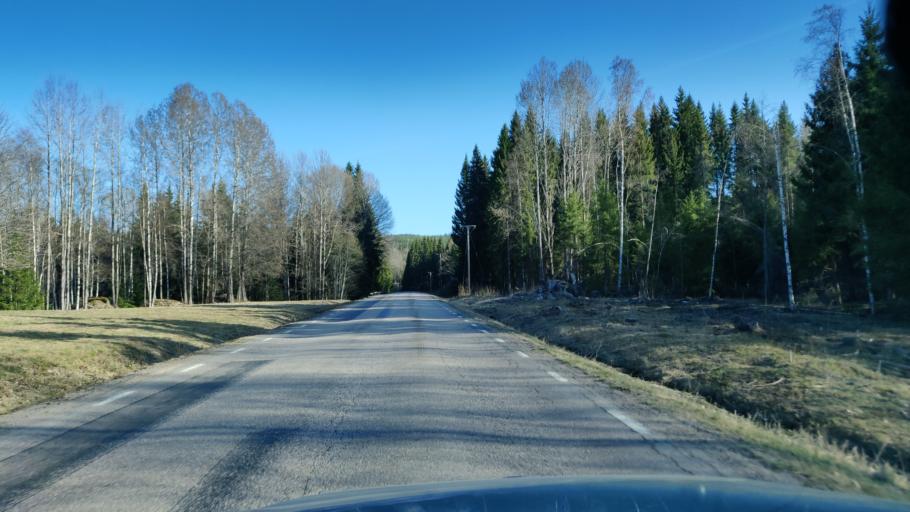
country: SE
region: Vaermland
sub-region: Munkfors Kommun
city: Munkfors
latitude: 59.9735
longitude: 13.4150
